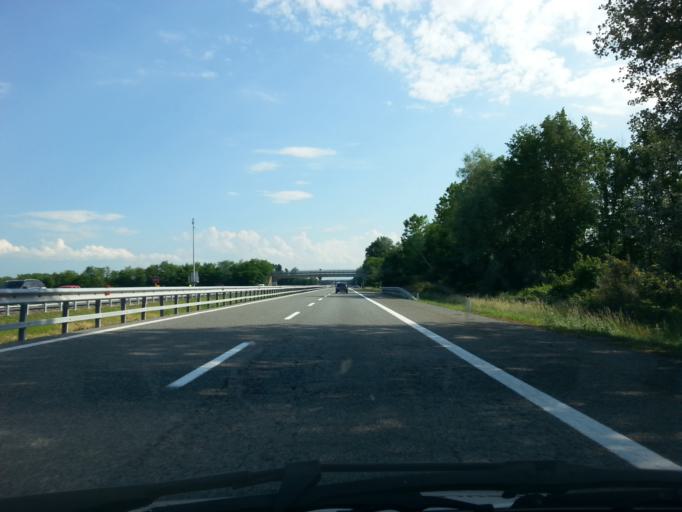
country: IT
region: Piedmont
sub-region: Provincia di Cuneo
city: Caramagna Piemonte
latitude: 44.7731
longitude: 7.7517
